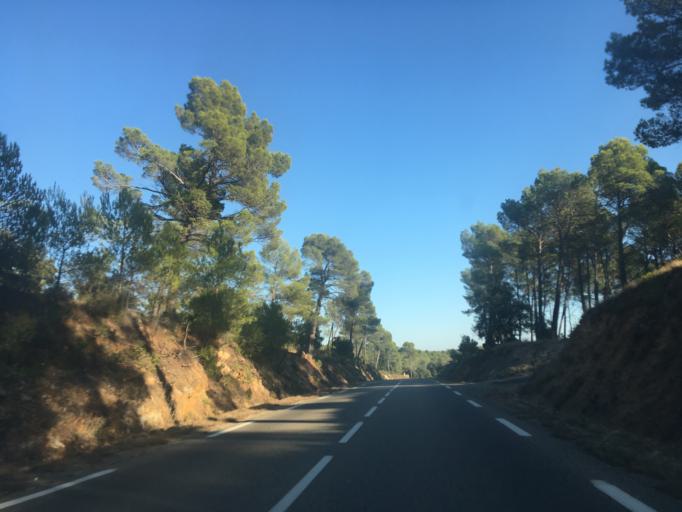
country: FR
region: Provence-Alpes-Cote d'Azur
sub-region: Departement du Var
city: Villecroze
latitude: 43.5968
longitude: 6.2506
